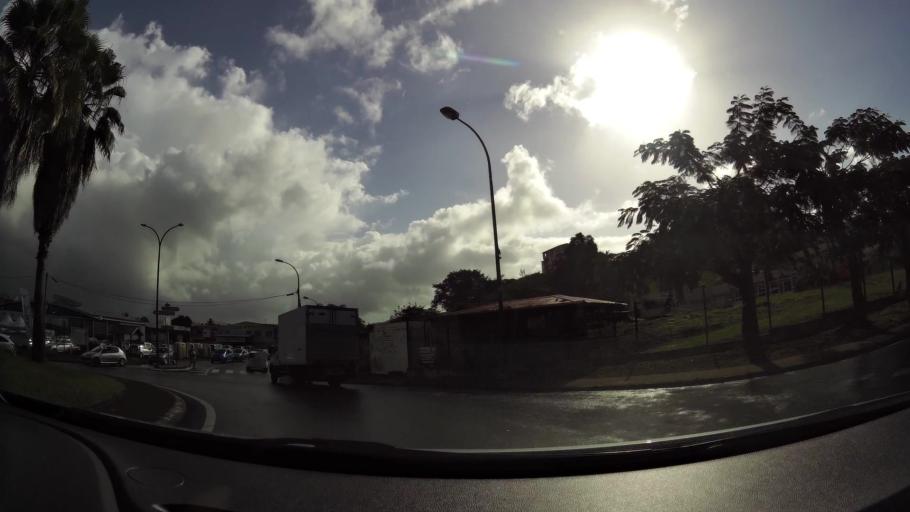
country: MQ
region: Martinique
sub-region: Martinique
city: Ducos
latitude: 14.5242
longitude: -60.9810
